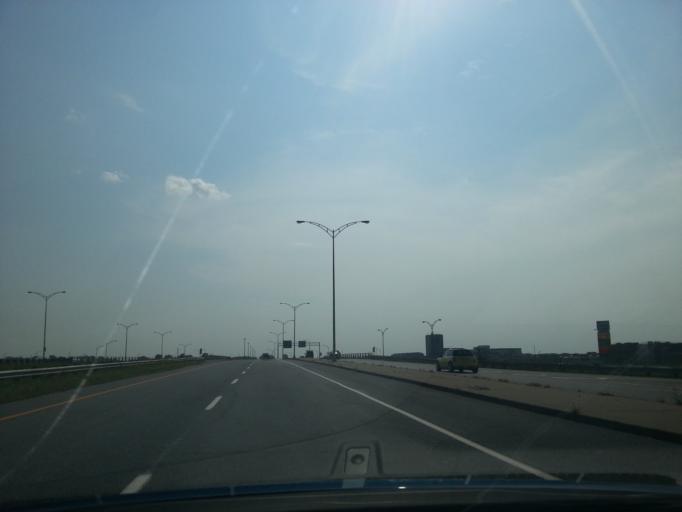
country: CA
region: Quebec
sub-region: Monteregie
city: Brossard
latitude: 45.4456
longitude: -73.4267
